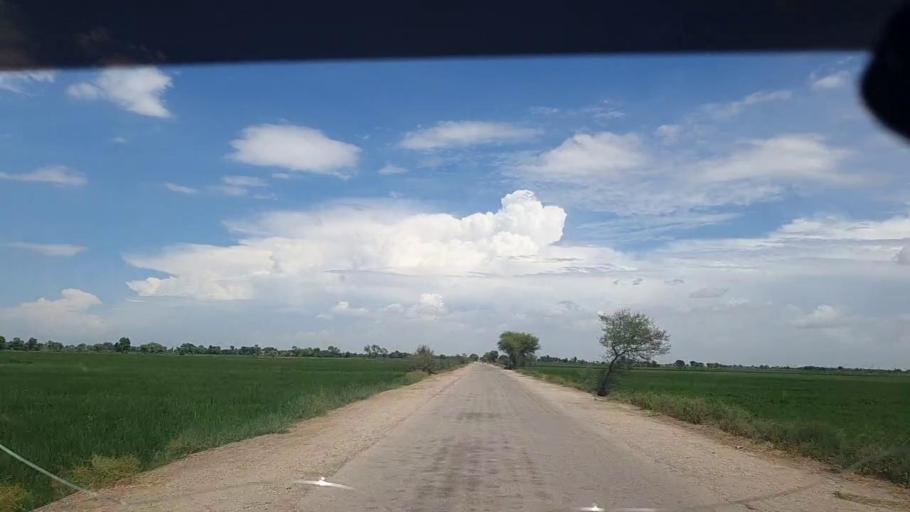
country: PK
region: Sindh
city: Ghauspur
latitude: 28.1556
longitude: 69.0066
